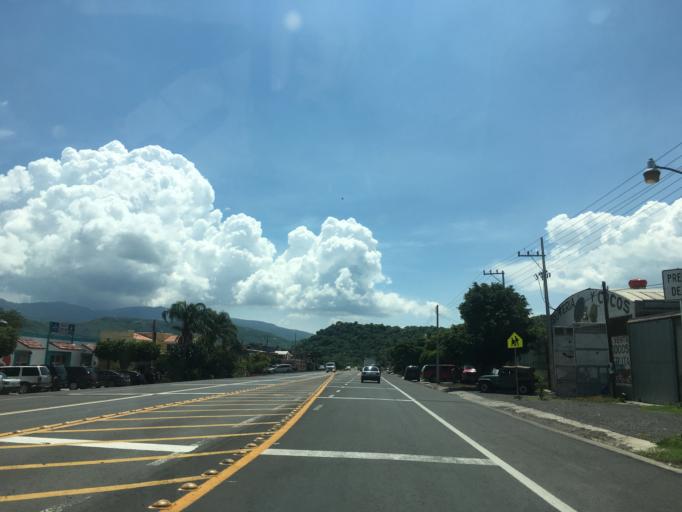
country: MX
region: Nayarit
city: Ixtlan del Rio
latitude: 21.0362
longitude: -104.4128
